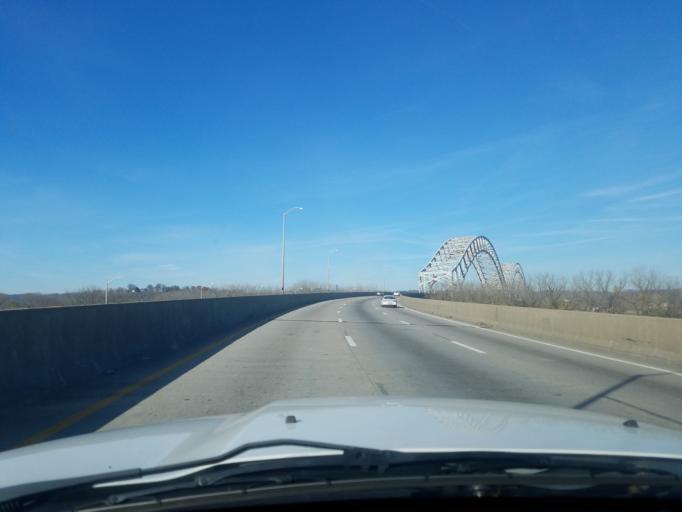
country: US
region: Indiana
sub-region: Floyd County
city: New Albany
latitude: 38.2754
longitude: -85.8177
